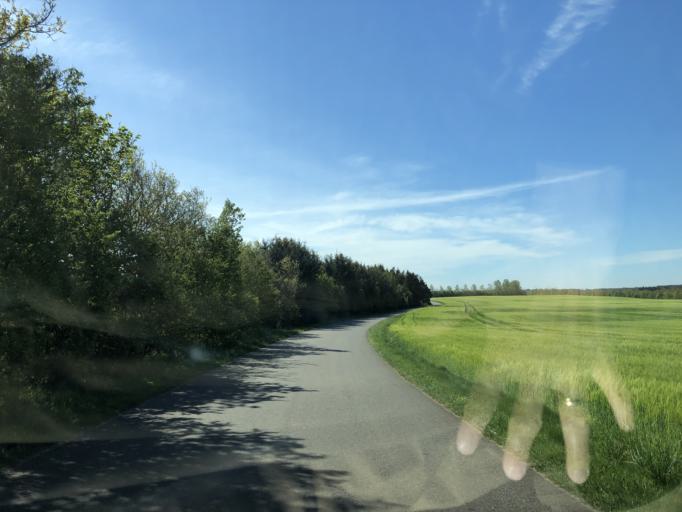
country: DK
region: Central Jutland
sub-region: Ringkobing-Skjern Kommune
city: Videbaek
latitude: 56.2012
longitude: 8.5129
